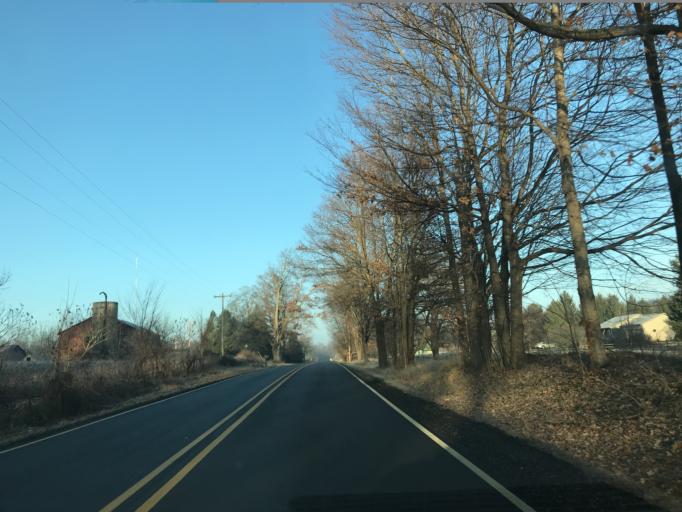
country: US
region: Michigan
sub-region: Ingham County
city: Leslie
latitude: 42.4400
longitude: -84.5526
